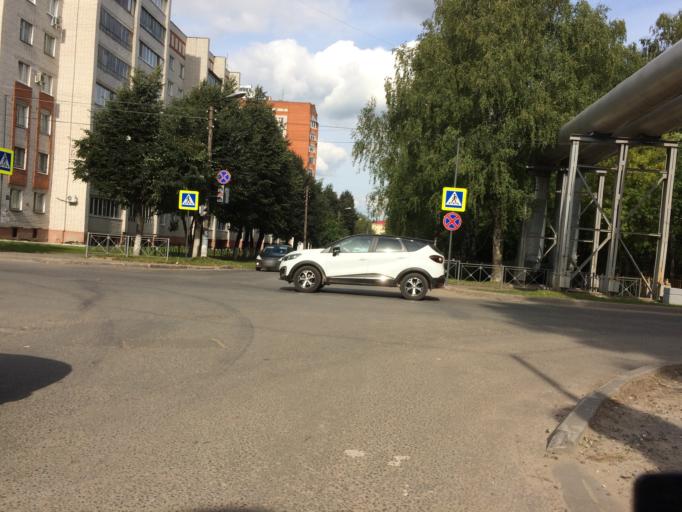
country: RU
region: Mariy-El
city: Yoshkar-Ola
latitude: 56.6316
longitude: 47.8760
